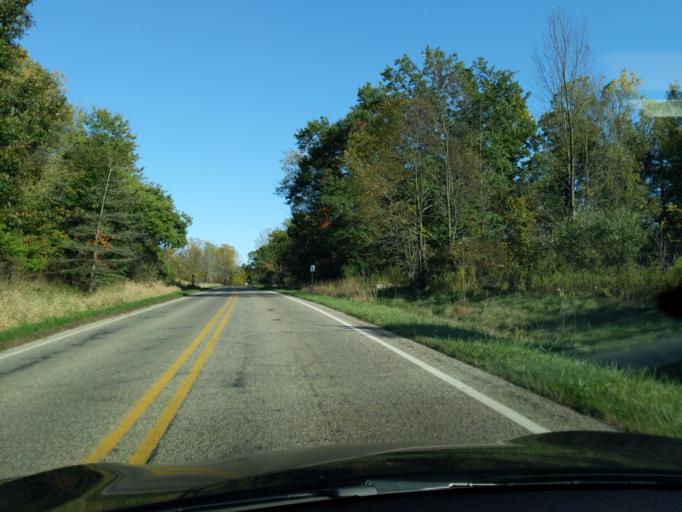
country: US
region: Michigan
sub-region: Shiawassee County
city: Laingsburg
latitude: 42.9249
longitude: -84.4153
